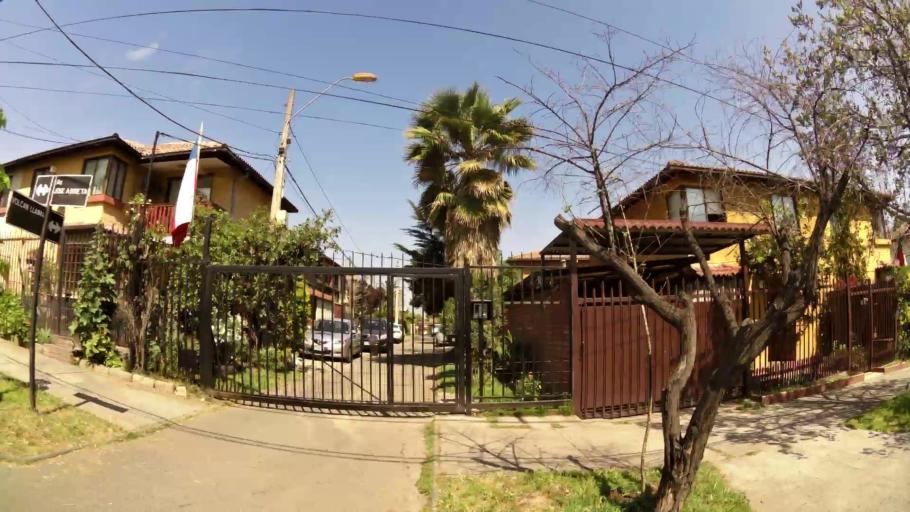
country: CL
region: Santiago Metropolitan
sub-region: Provincia de Santiago
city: Villa Presidente Frei, Nunoa, Santiago, Chile
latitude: -33.4635
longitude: -70.5386
